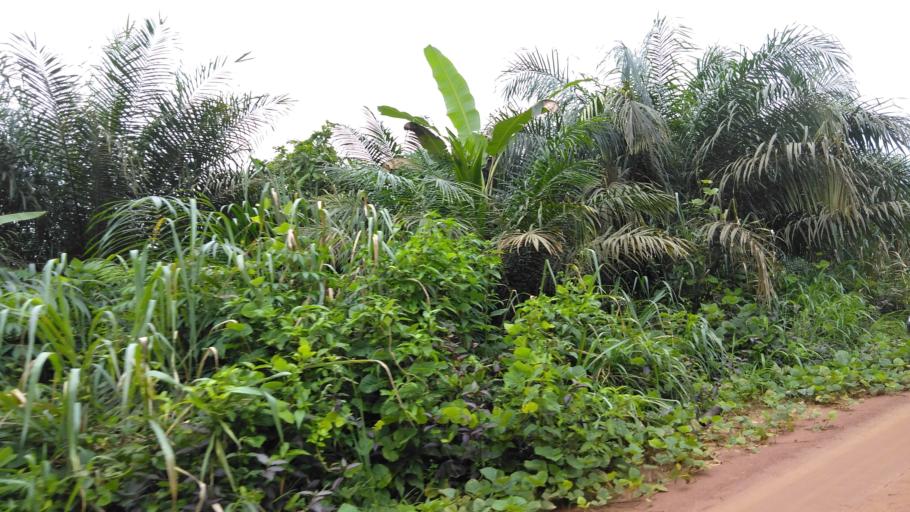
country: NG
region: Ogun
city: Abigi
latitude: 6.5843
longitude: 4.5580
